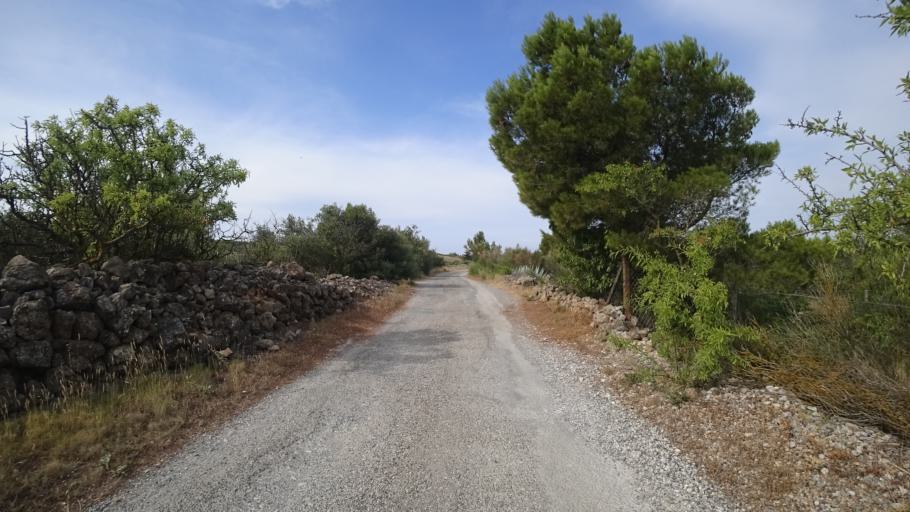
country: FR
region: Languedoc-Roussillon
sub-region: Departement de l'Aude
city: Leucate
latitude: 42.9021
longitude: 3.0200
